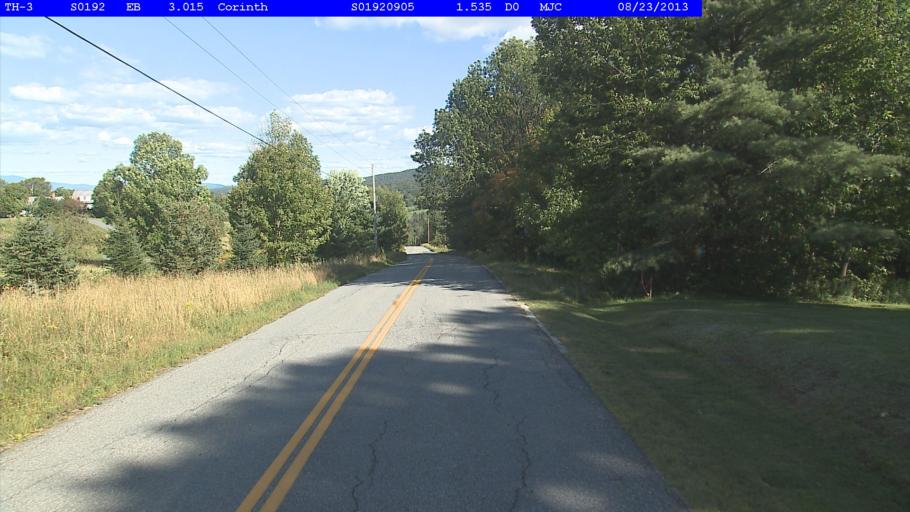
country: US
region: Vermont
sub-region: Orange County
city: Chelsea
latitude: 44.0055
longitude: -72.3277
